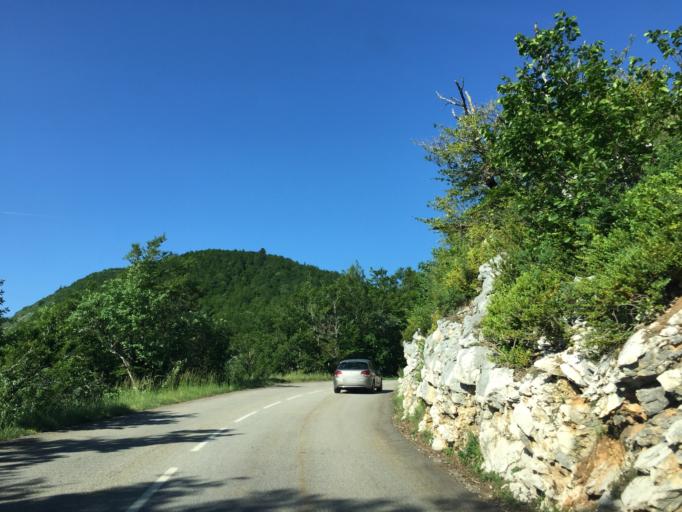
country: FR
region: Rhone-Alpes
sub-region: Departement de la Drome
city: Saint-Laurent-en-Royans
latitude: 44.9076
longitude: 5.3610
